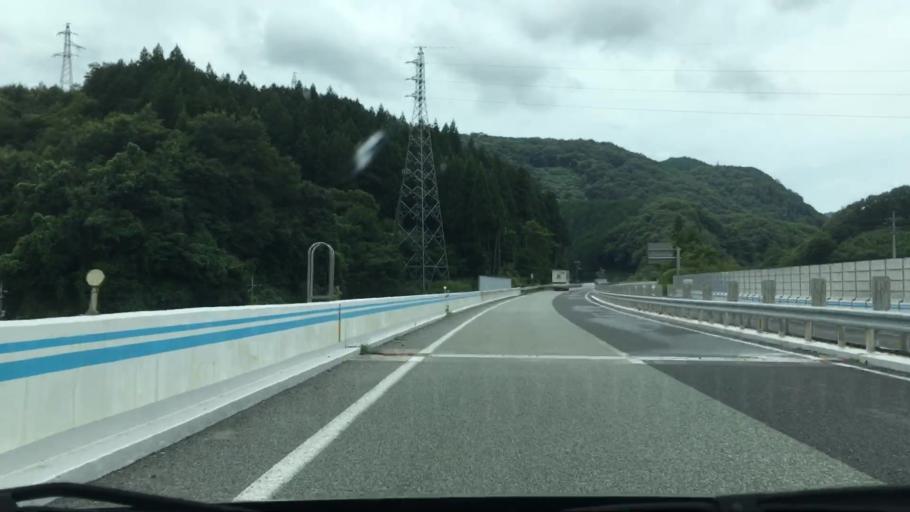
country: JP
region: Okayama
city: Niimi
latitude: 34.8866
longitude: 133.2763
